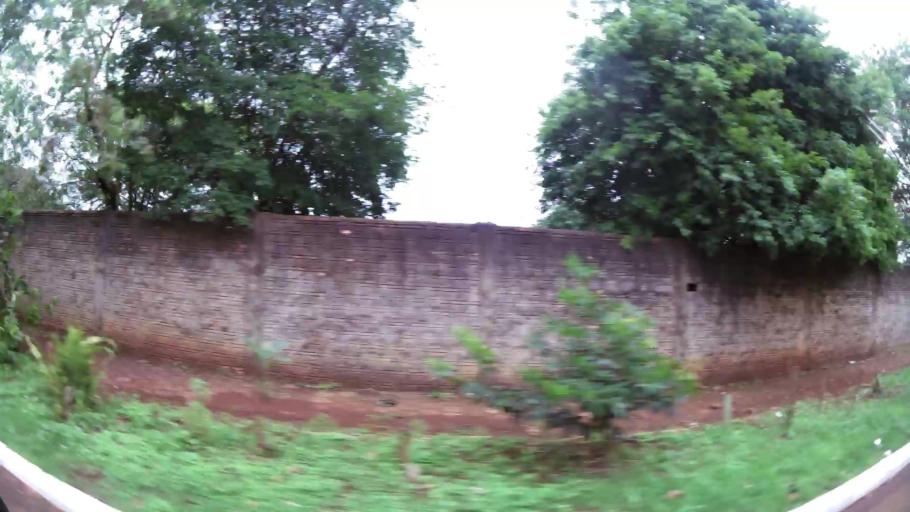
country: PY
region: Alto Parana
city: Ciudad del Este
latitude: -25.4837
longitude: -54.7604
